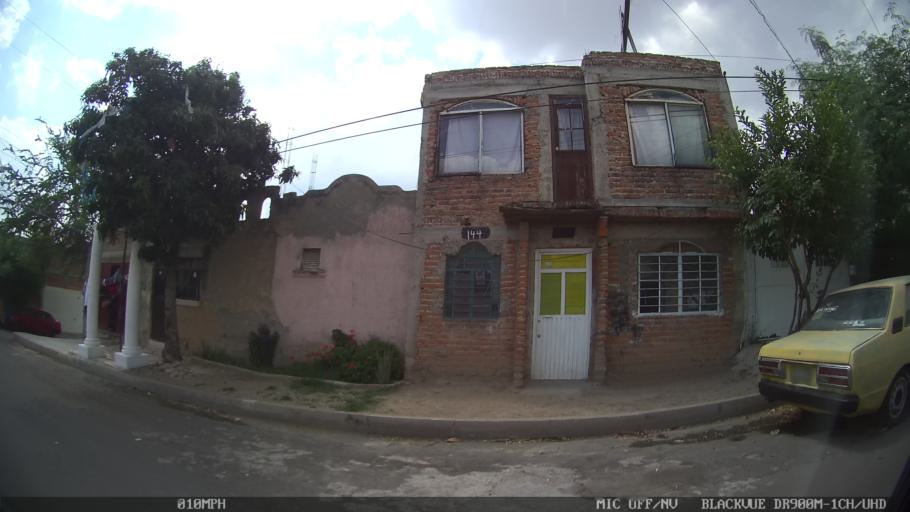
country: MX
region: Jalisco
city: Tlaquepaque
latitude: 20.6268
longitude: -103.2694
